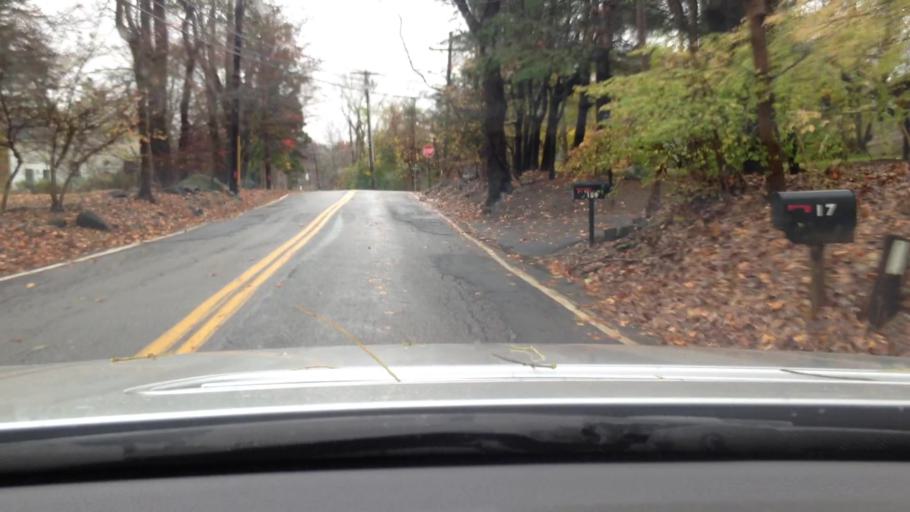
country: US
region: New York
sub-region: Westchester County
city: Croton-on-Hudson
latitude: 41.2272
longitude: -73.8769
